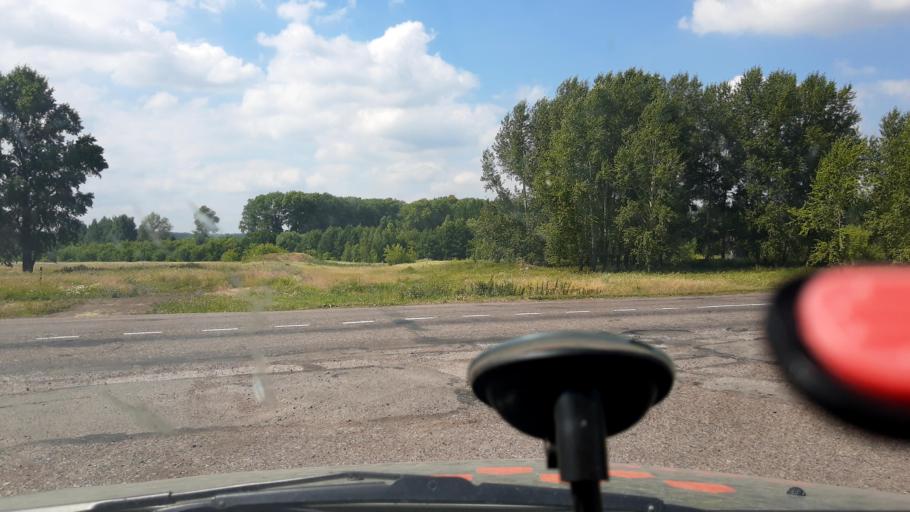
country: RU
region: Bashkortostan
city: Chekmagush
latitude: 54.8893
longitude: 54.5784
